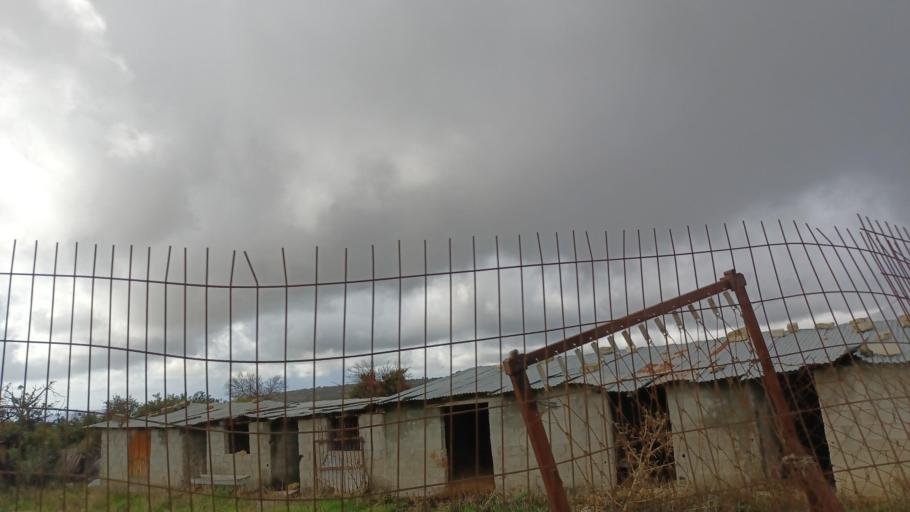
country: CY
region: Limassol
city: Sotira
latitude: 34.7468
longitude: 32.8409
